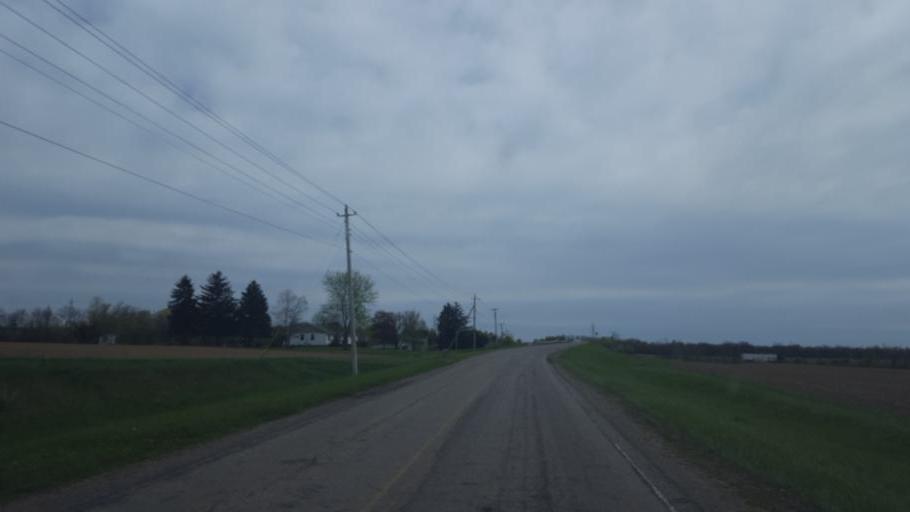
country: US
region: Ohio
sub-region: Crawford County
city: Crestline
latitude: 40.7651
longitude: -82.6982
